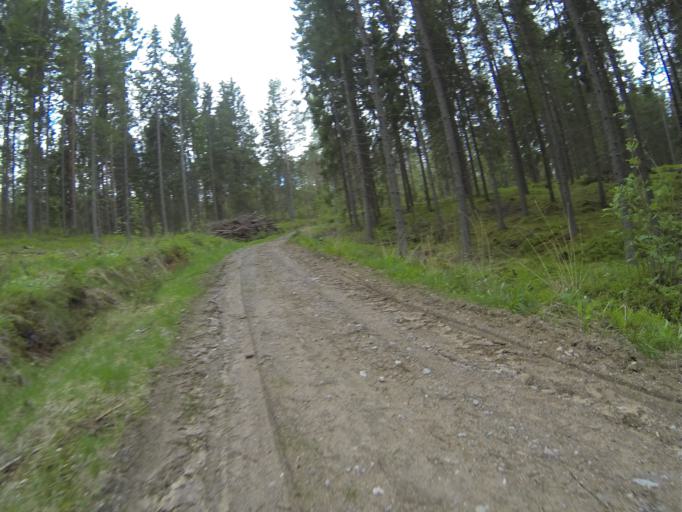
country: FI
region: Varsinais-Suomi
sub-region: Salo
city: Halikko
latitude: 60.3375
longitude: 23.0824
